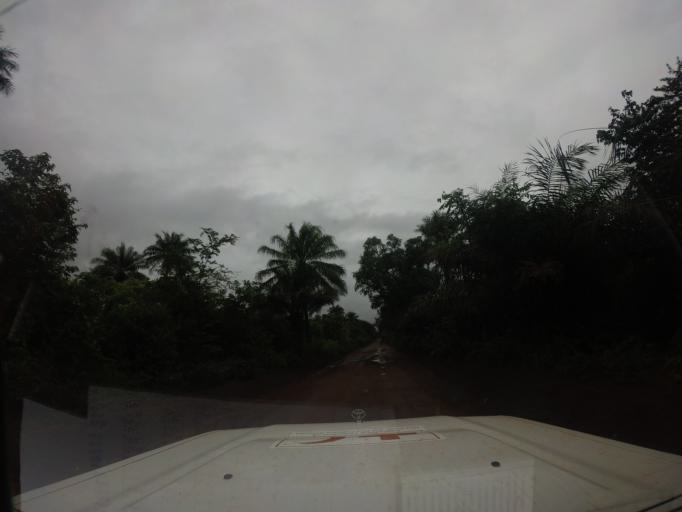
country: SL
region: Northern Province
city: Kambia
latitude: 9.1778
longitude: -12.8784
